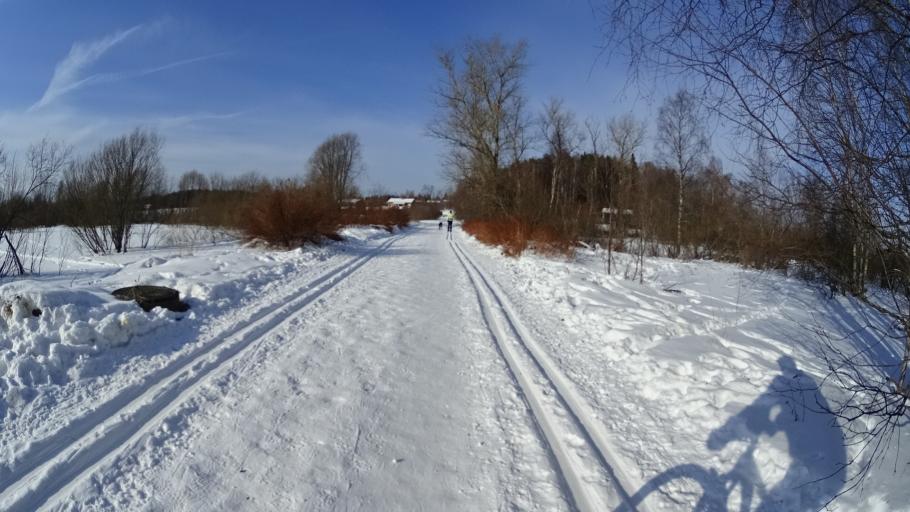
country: FI
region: Uusimaa
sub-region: Helsinki
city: Kauniainen
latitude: 60.2468
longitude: 24.7303
